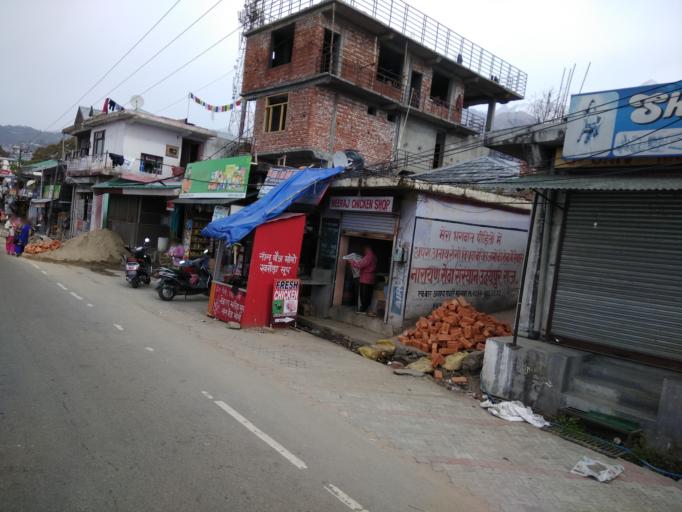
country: IN
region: Himachal Pradesh
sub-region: Kangra
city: Dharmsala
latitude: 32.1997
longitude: 76.3363
